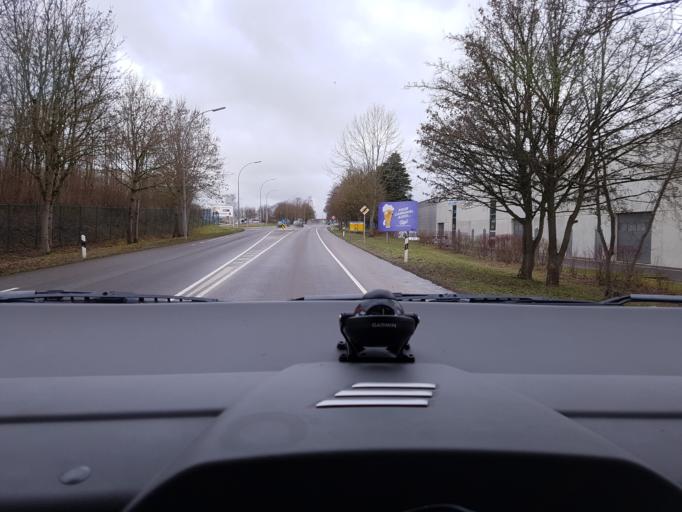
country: LU
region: Luxembourg
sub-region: Canton de Capellen
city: Koerich
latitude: 49.6467
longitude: 5.9606
